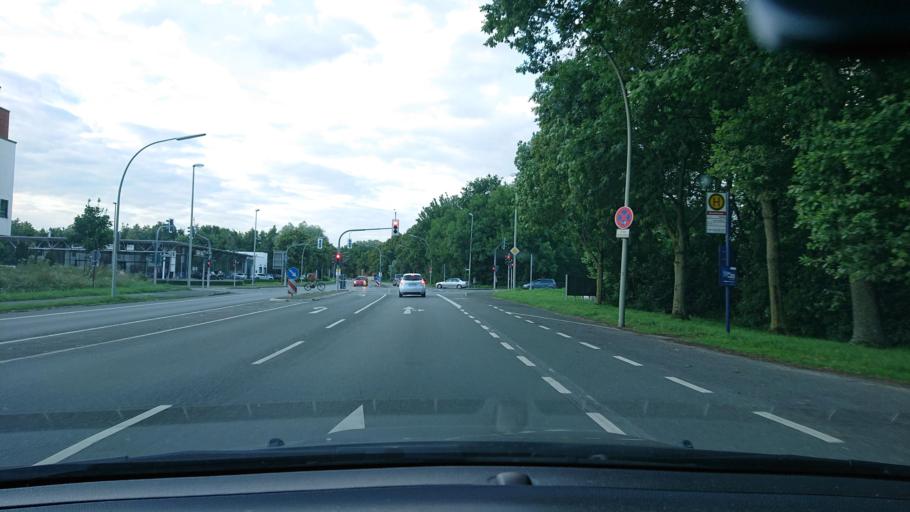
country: DE
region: North Rhine-Westphalia
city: Werne
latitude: 51.6676
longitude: 7.6349
